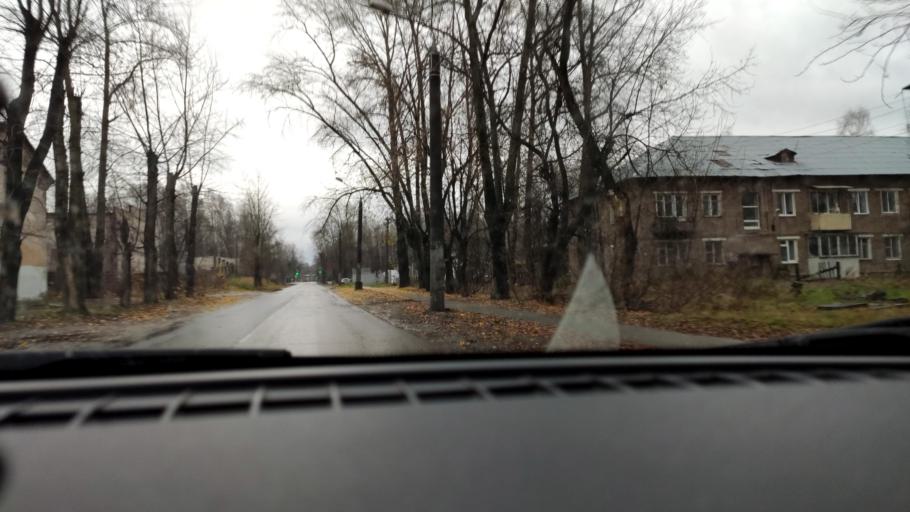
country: RU
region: Perm
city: Perm
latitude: 58.0930
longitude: 56.3790
